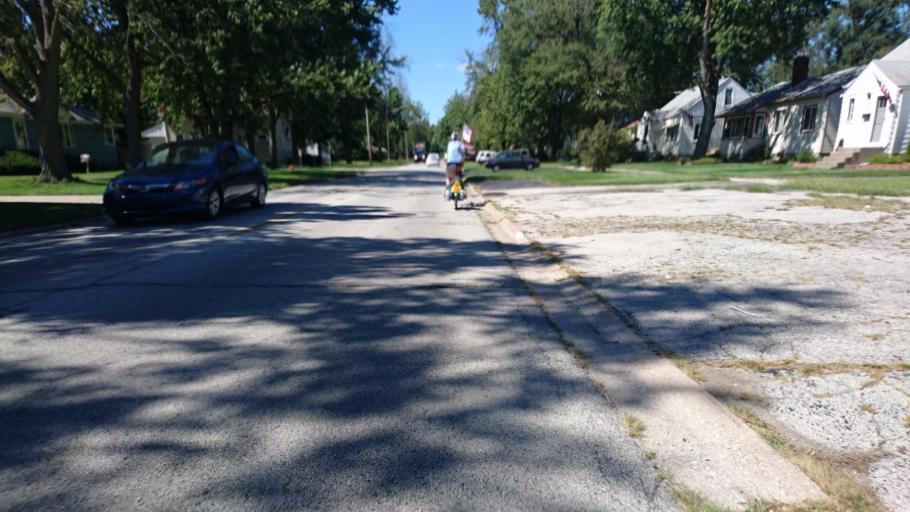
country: US
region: Illinois
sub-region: Cook County
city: Lansing
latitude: 41.5576
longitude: -87.5314
